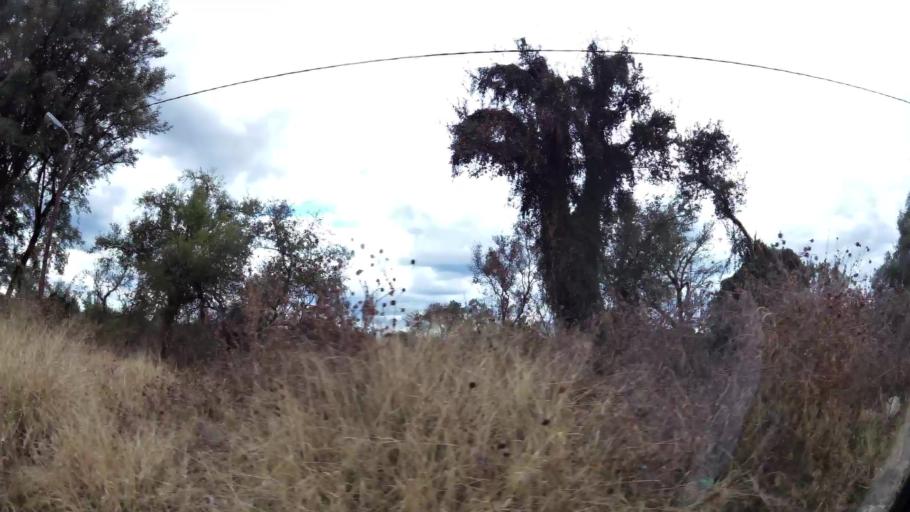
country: ZA
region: Limpopo
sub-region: Waterberg District Municipality
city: Modimolle
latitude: -24.7021
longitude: 28.4187
